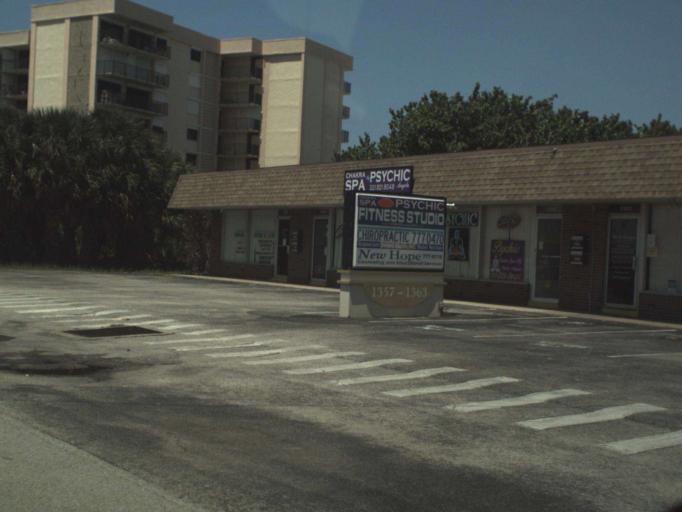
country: US
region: Florida
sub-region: Brevard County
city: Satellite Beach
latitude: 28.1737
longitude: -80.5897
